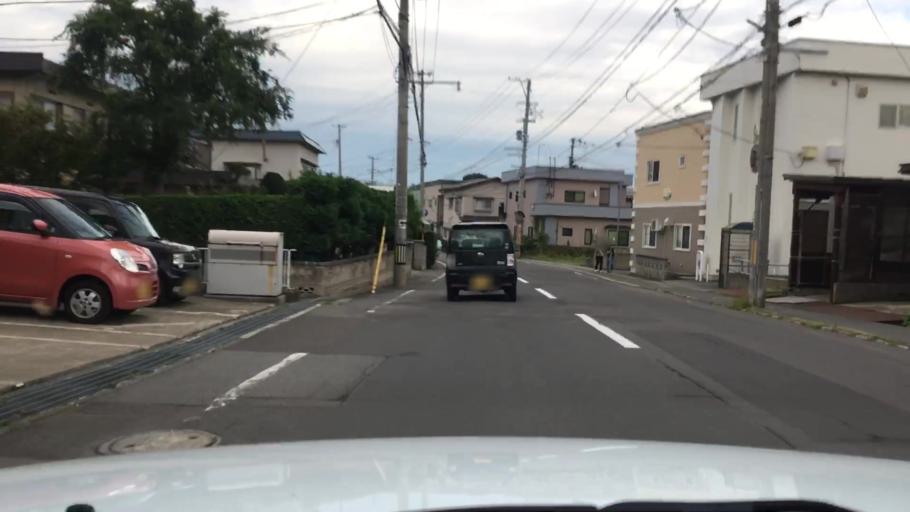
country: JP
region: Aomori
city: Hirosaki
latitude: 40.5848
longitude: 140.4718
